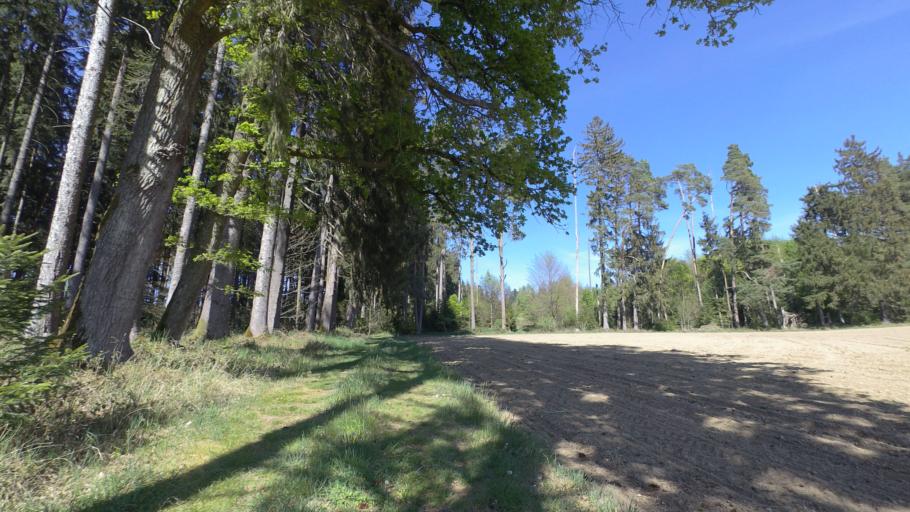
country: DE
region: Bavaria
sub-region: Upper Bavaria
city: Traunreut
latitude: 47.9447
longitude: 12.5577
